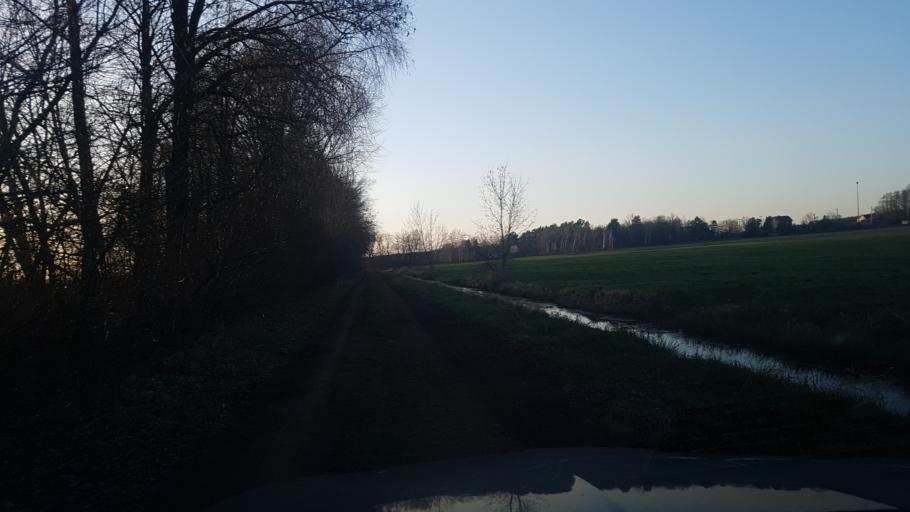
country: DE
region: Brandenburg
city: Bad Liebenwerda
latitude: 51.5323
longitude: 13.3466
